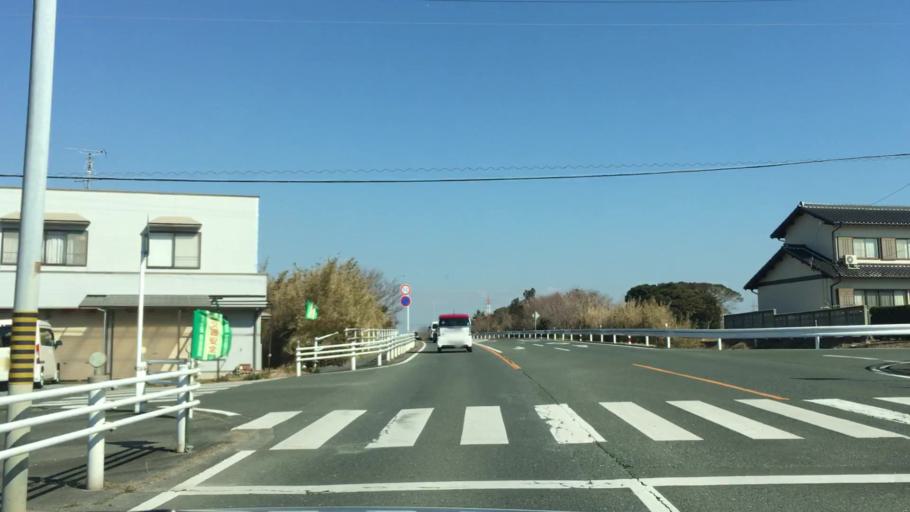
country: JP
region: Aichi
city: Tahara
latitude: 34.6667
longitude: 137.2855
